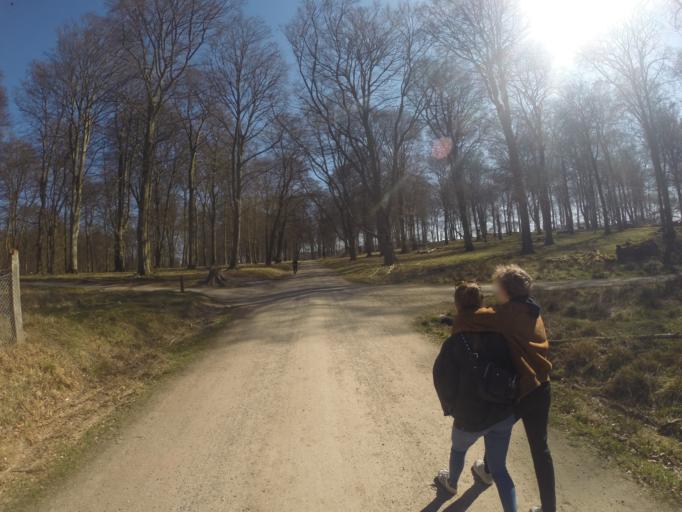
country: DK
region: Capital Region
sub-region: Rudersdal Kommune
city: Trorod
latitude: 55.8031
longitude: 12.5636
